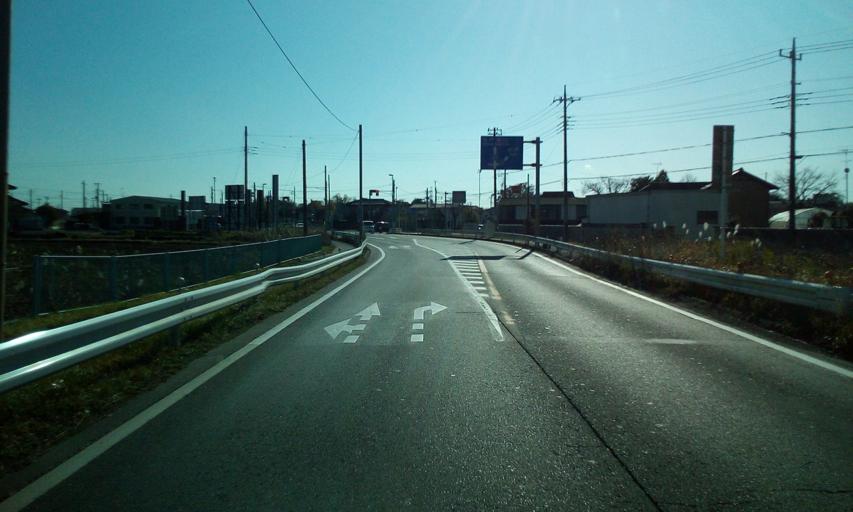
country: JP
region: Ibaraki
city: Sakai
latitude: 36.0948
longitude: 139.7893
